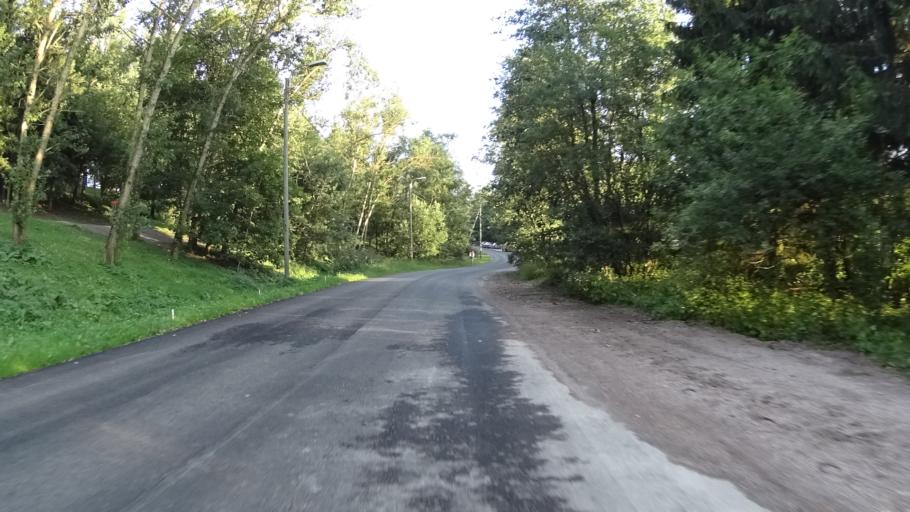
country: FI
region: Uusimaa
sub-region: Helsinki
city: Teekkarikylae
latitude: 60.2154
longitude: 24.8465
